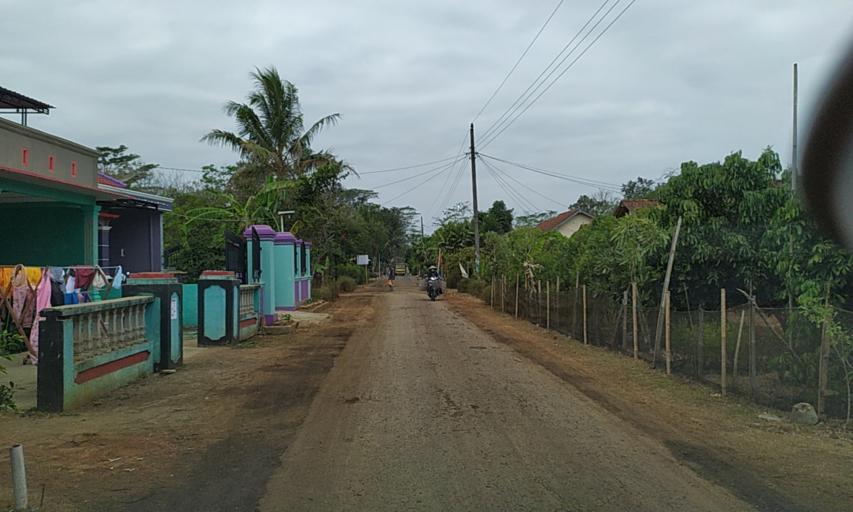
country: ID
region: Central Java
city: Kroya
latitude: -7.6672
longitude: 109.3043
